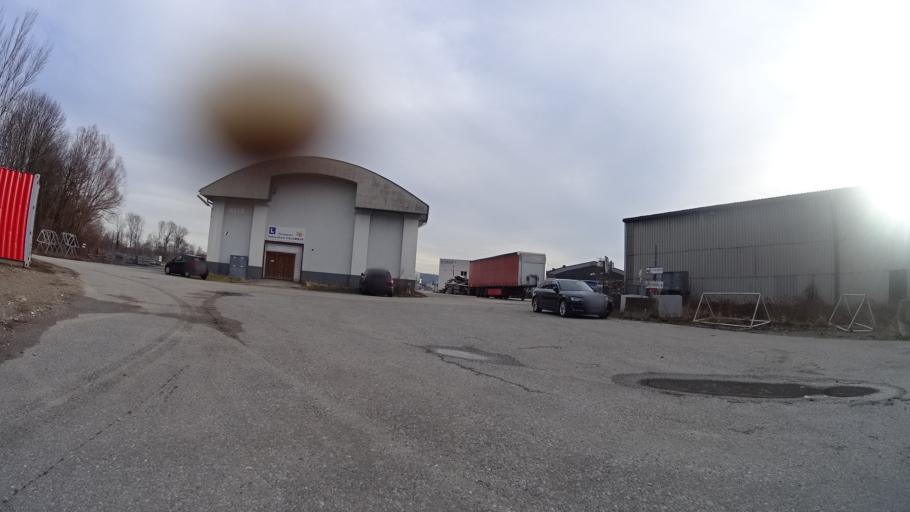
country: AT
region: Lower Austria
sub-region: Politischer Bezirk Korneuburg
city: Korneuburg
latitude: 48.3440
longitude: 16.3167
